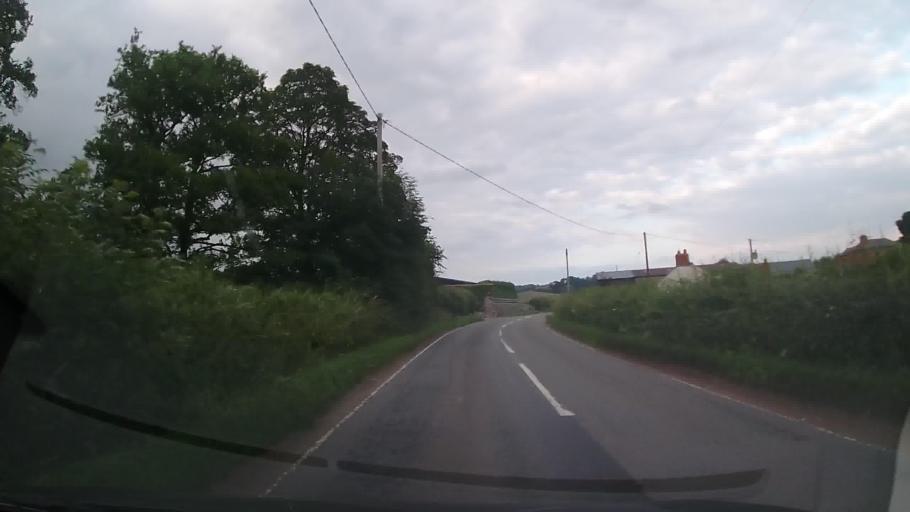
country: GB
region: Wales
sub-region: Sir Powys
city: Llanfechain
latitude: 52.8068
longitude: -3.1666
